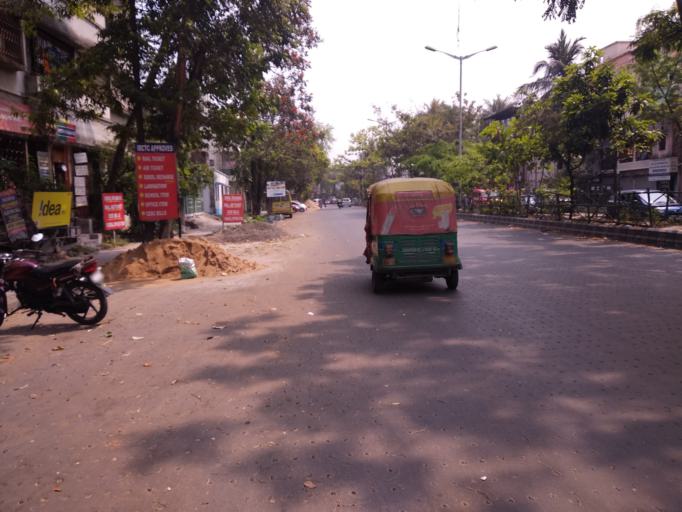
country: IN
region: West Bengal
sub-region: Kolkata
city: Kolkata
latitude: 22.5036
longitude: 88.3765
